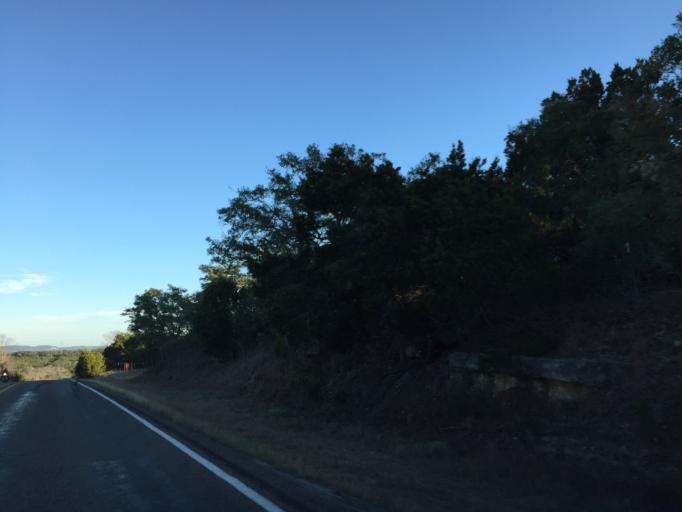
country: US
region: Texas
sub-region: Travis County
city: Lago Vista
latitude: 30.5213
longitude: -98.0786
